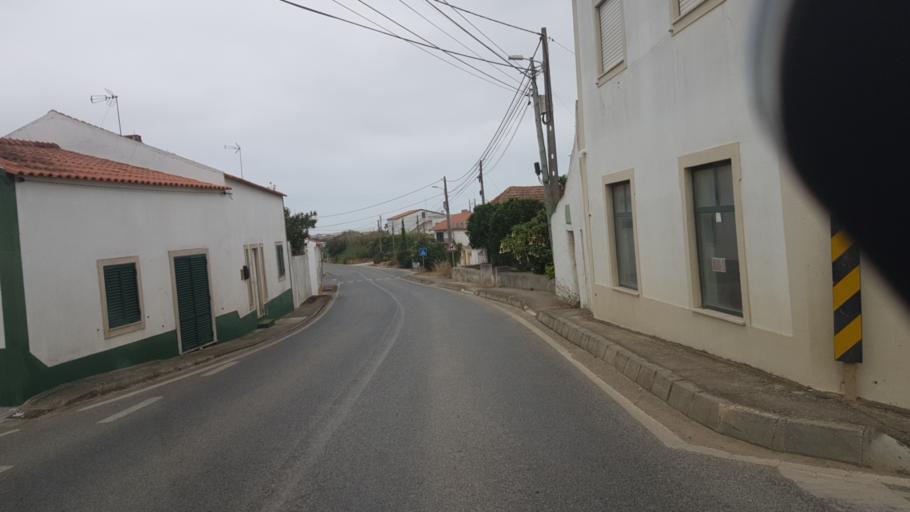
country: PT
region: Leiria
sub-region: Peniche
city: Atouguia da Baleia
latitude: 39.3378
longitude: -9.3152
